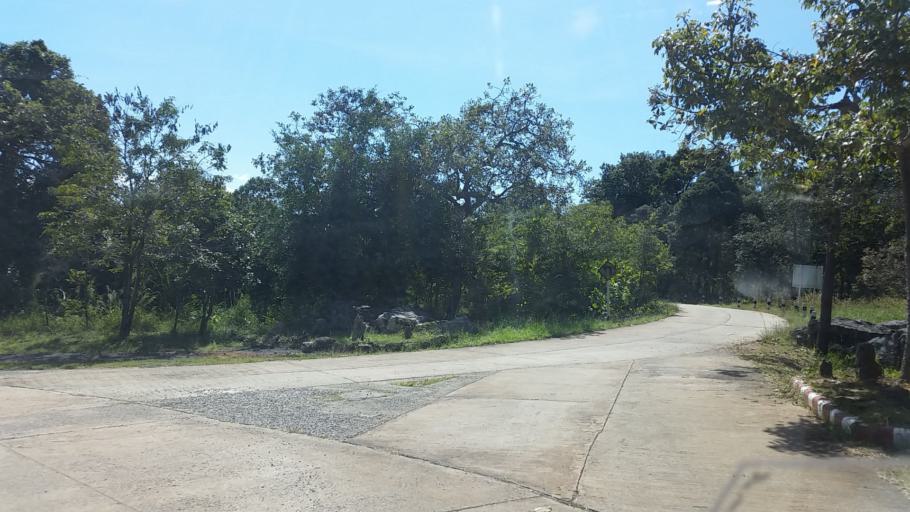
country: TH
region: Chaiyaphum
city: Sap Yai
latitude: 15.6359
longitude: 101.3923
